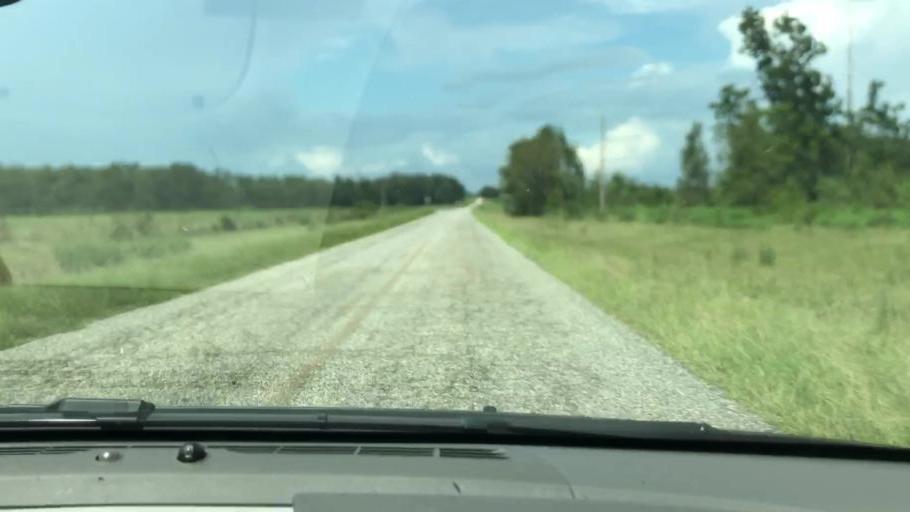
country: US
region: Georgia
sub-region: Seminole County
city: Donalsonville
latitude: 31.1795
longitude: -85.0045
